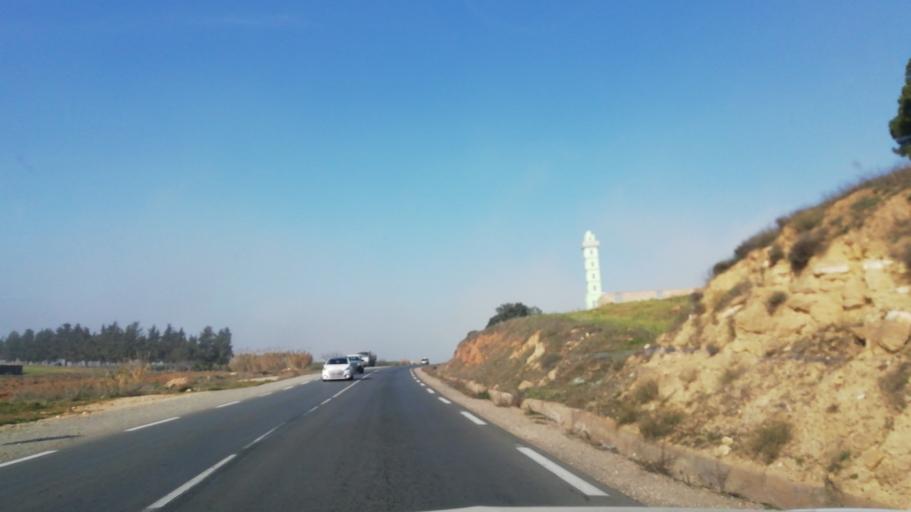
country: DZ
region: Mascara
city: Mascara
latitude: 35.5253
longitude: 0.3482
